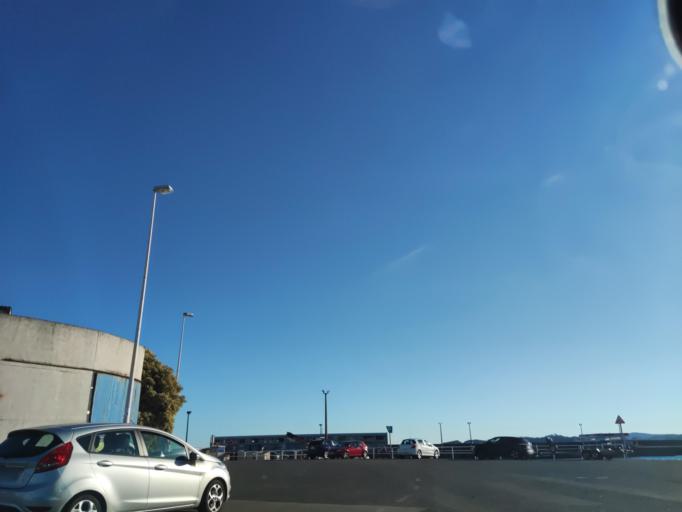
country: ES
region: Galicia
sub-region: Provincia da Coruna
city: Boiro
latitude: 42.6147
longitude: -8.8877
